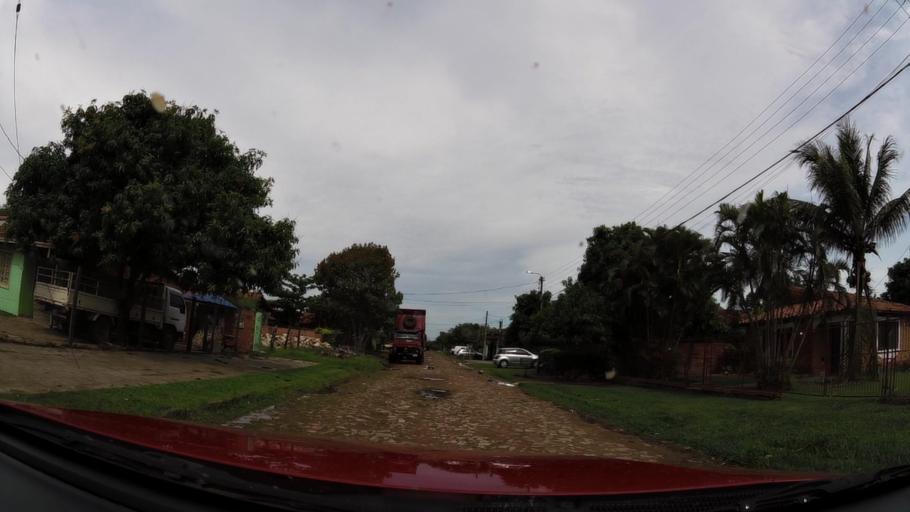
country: PY
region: Central
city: Limpio
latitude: -25.1653
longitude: -57.4813
